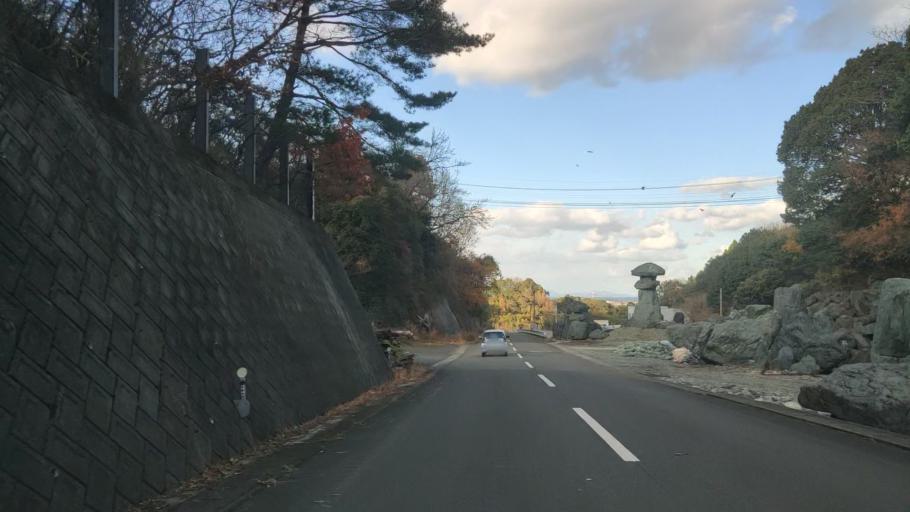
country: JP
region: Ehime
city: Saijo
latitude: 33.8852
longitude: 133.1292
